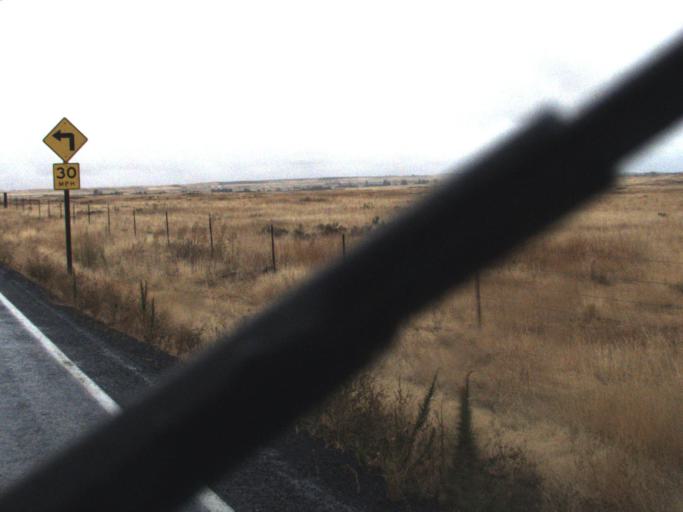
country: US
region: Washington
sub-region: Lincoln County
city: Davenport
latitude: 47.3319
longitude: -117.9833
